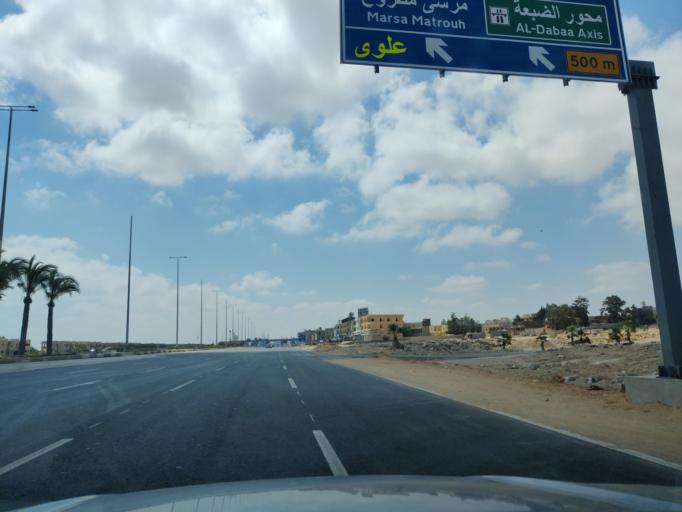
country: EG
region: Muhafazat Matruh
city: Al `Alamayn
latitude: 30.8435
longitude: 28.9453
